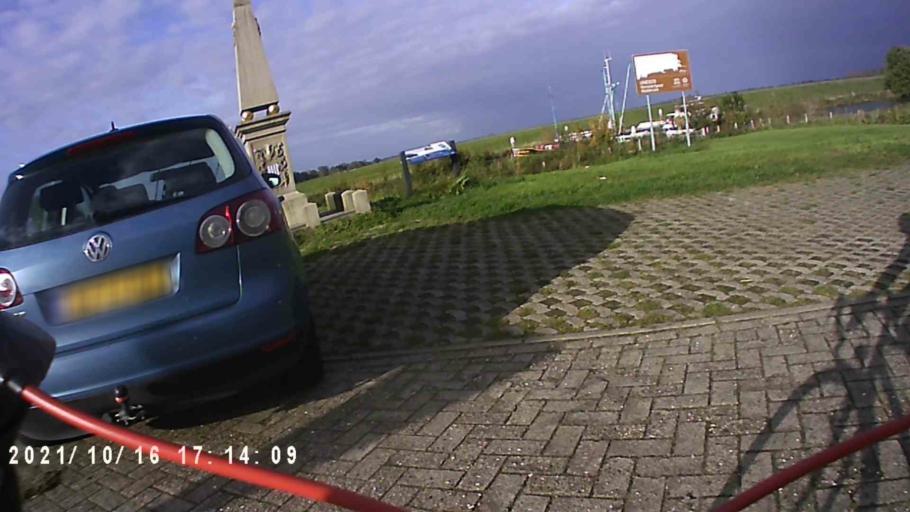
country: NL
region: Friesland
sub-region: Gemeente Kollumerland en Nieuwkruisland
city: Kollum
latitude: 53.3179
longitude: 6.1586
